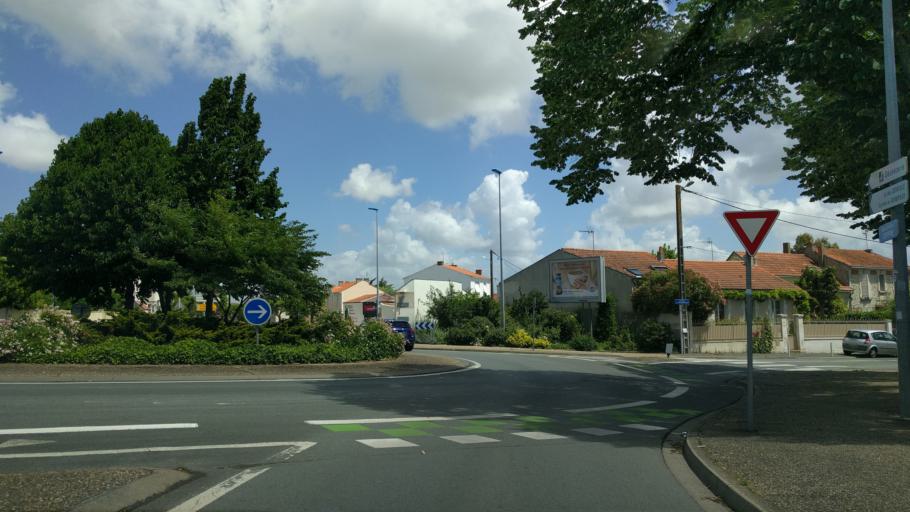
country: FR
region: Poitou-Charentes
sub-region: Departement de la Charente-Maritime
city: La Rochelle
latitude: 46.1613
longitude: -1.1399
